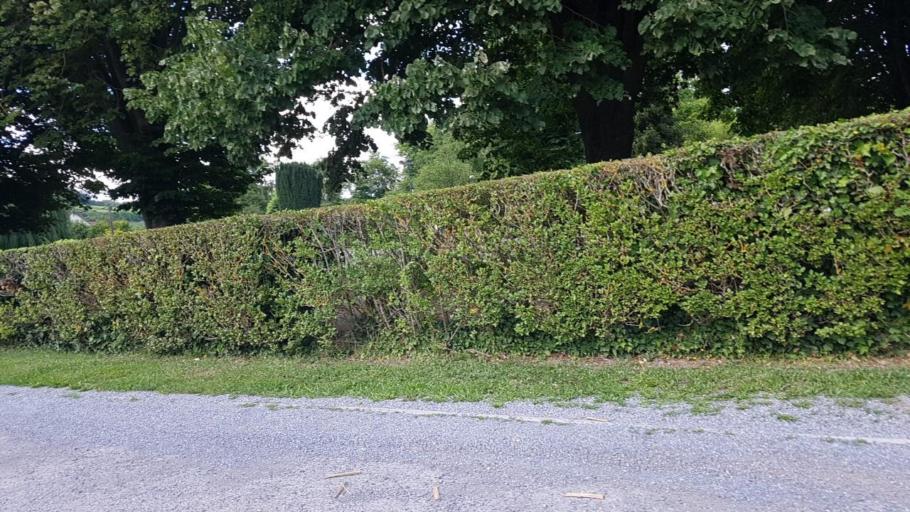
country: FR
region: Picardie
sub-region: Departement de l'Aisne
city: Crezancy
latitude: 49.0859
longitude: 3.5353
